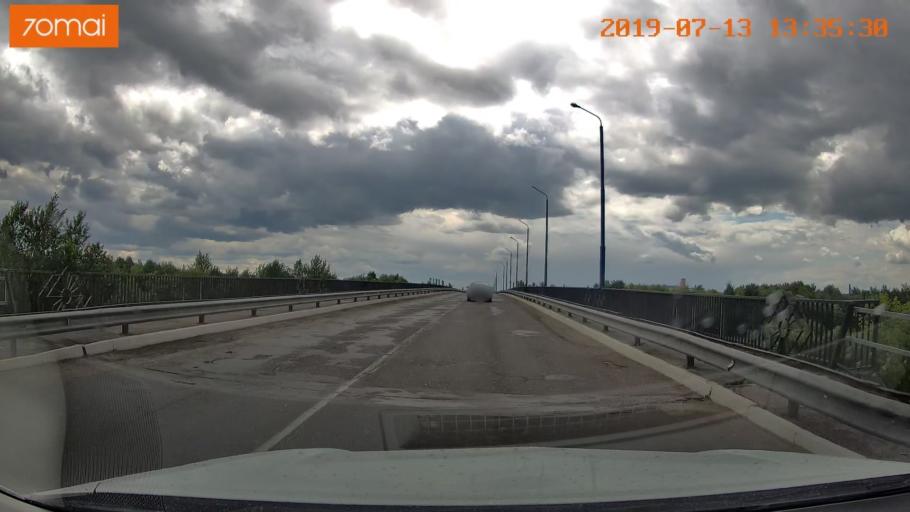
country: BY
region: Mogilev
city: Asipovichy
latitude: 53.3069
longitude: 28.6257
